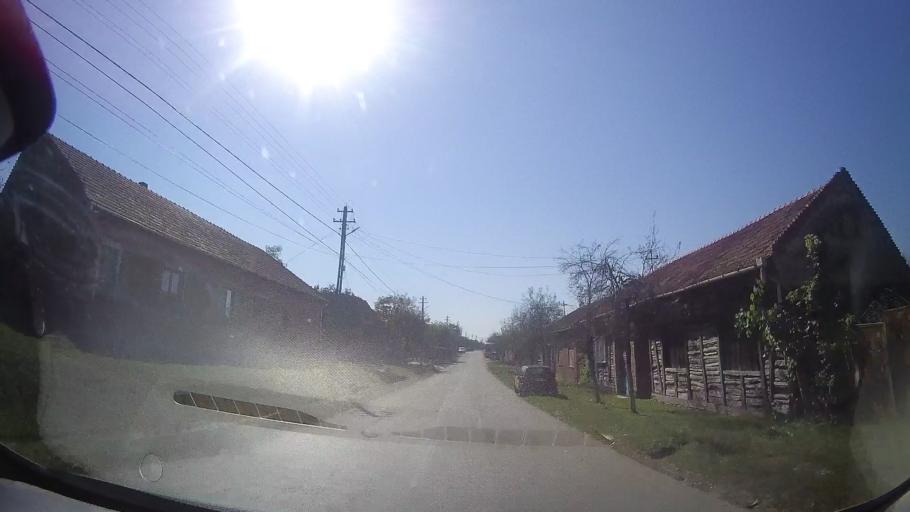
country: RO
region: Timis
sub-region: Comuna Bethausen
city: Bethausen
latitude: 45.8625
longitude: 21.9701
